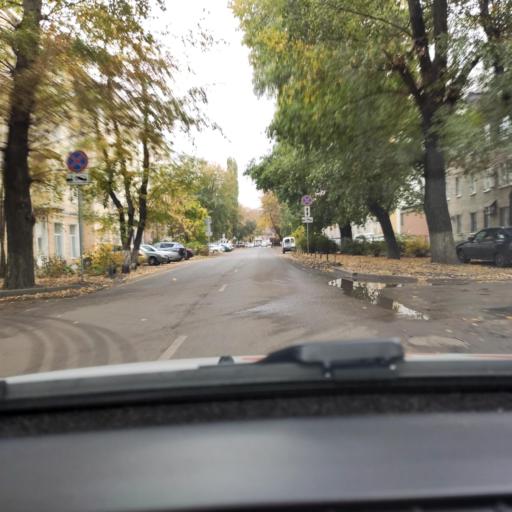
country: RU
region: Voronezj
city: Voronezh
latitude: 51.6609
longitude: 39.1827
